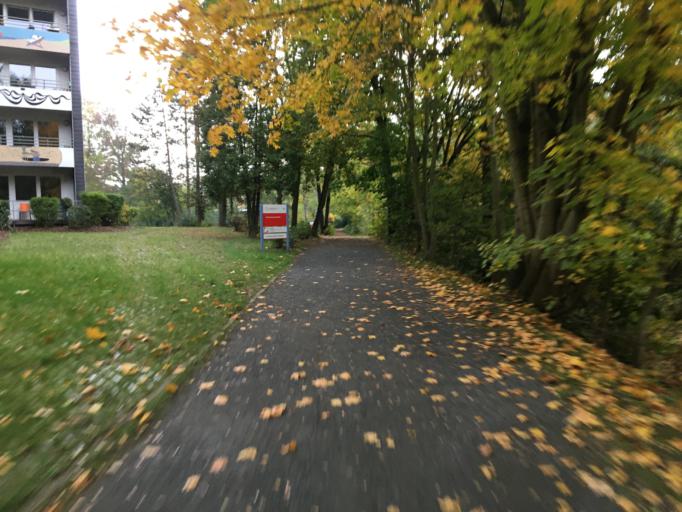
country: DE
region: Lower Saxony
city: Braunschweig
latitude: 52.2998
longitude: 10.5460
